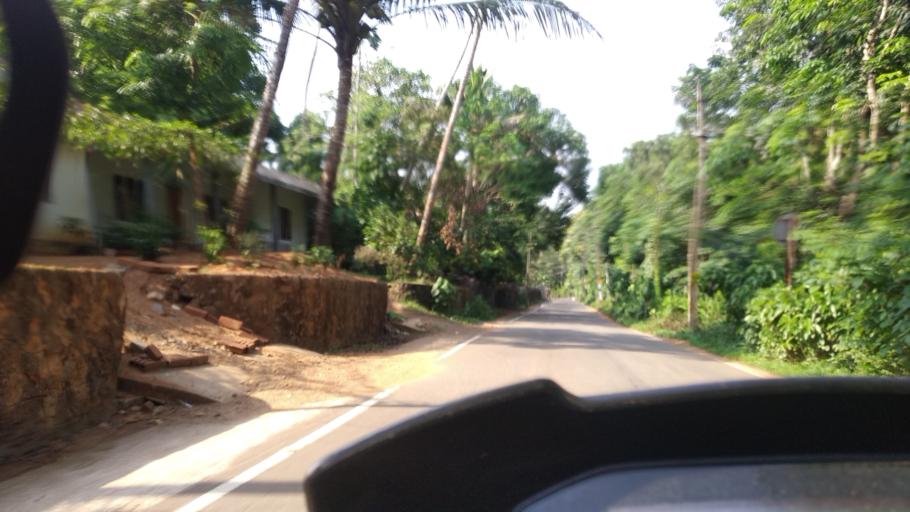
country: IN
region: Kerala
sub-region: Ernakulam
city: Piravam
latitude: 9.8479
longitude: 76.5344
